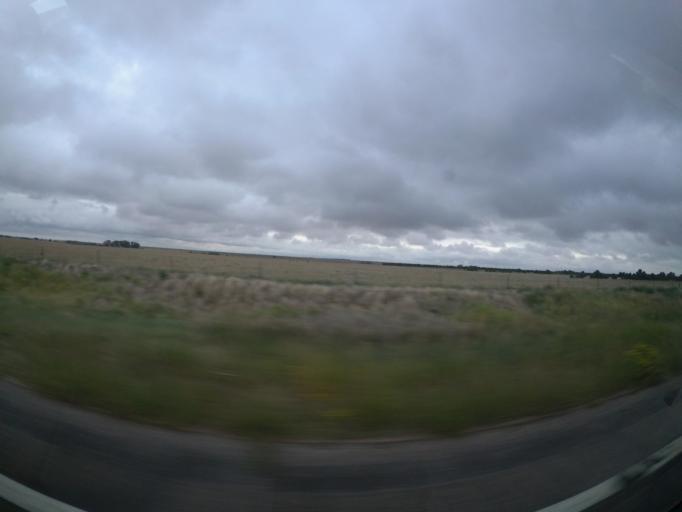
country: US
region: Colorado
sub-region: Yuma County
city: Yuma
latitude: 39.6702
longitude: -102.8773
